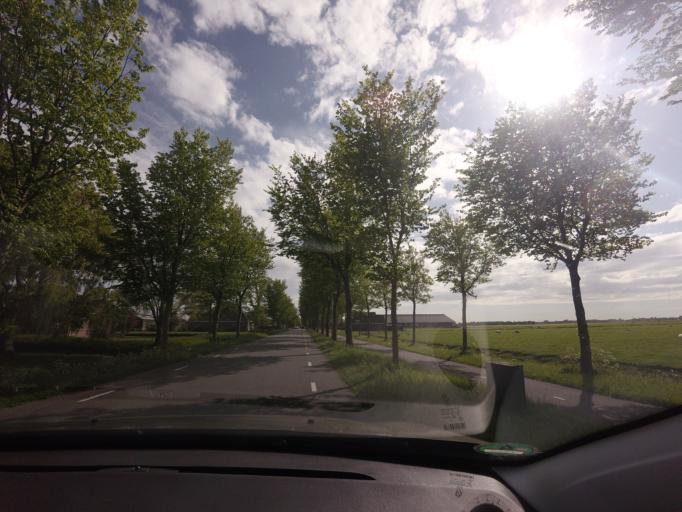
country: NL
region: North Holland
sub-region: Gemeente Beemster
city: Halfweg
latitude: 52.5601
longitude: 4.9200
